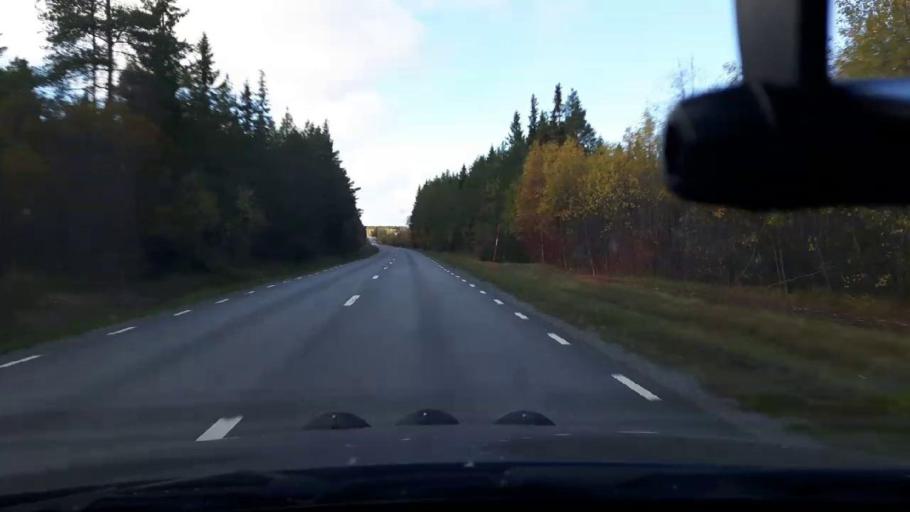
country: SE
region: Jaemtland
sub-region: Bergs Kommun
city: Hoverberg
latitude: 62.9819
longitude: 14.4496
